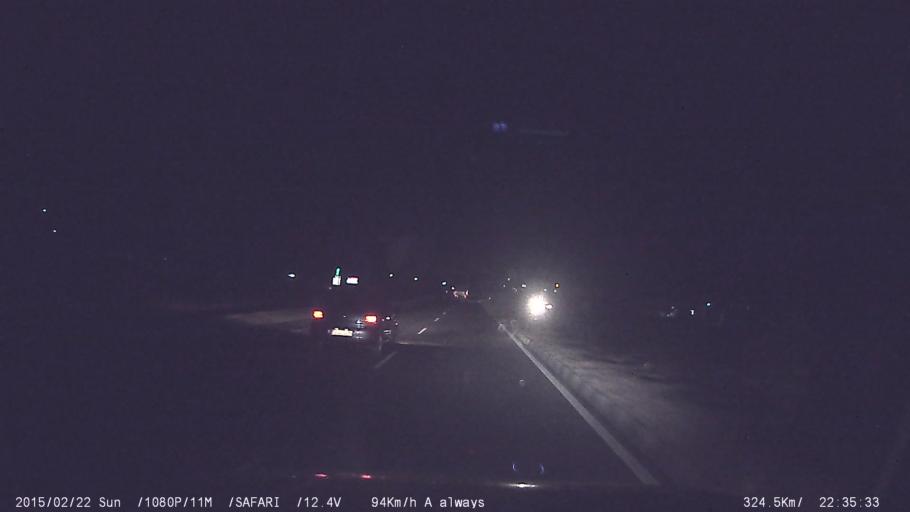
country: IN
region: Tamil Nadu
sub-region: Namakkal
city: Velur
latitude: 11.1348
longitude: 78.0186
